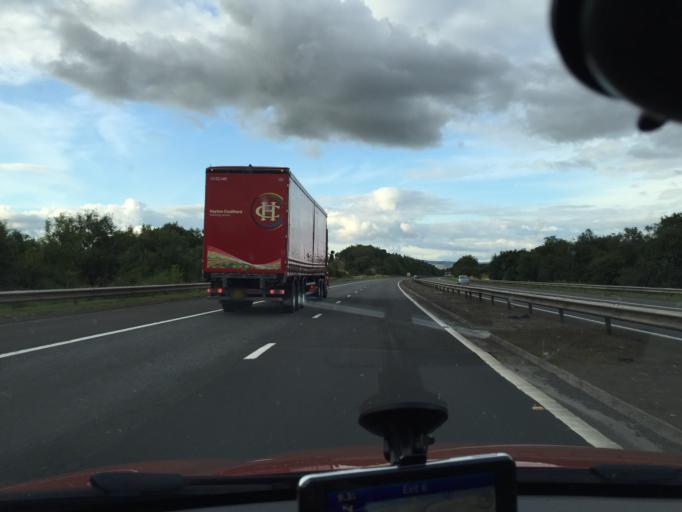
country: GB
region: Scotland
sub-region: North Lanarkshire
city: Glenboig
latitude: 55.9031
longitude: -4.0681
